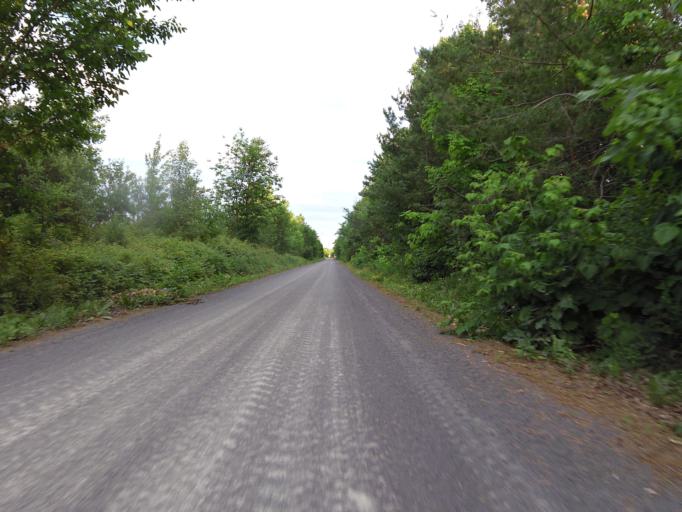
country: CA
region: Ontario
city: Arnprior
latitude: 45.3368
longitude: -76.2960
